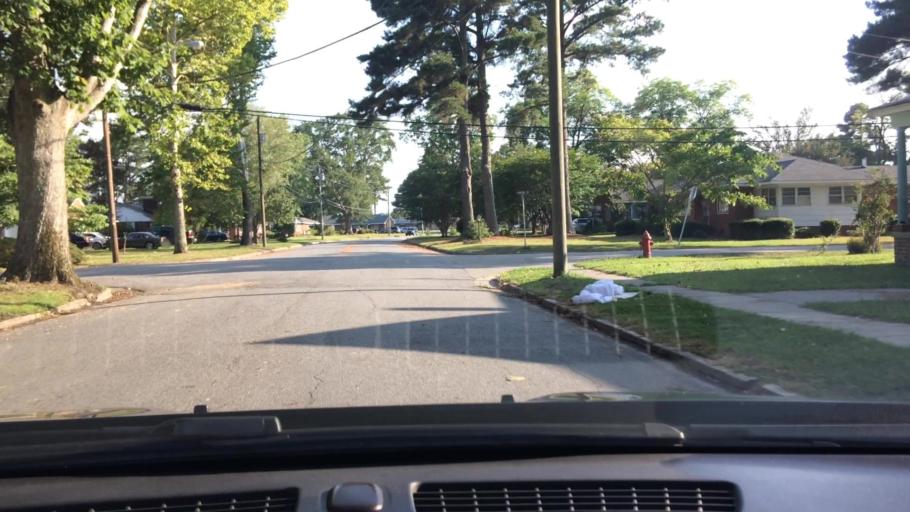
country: US
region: North Carolina
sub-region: Pitt County
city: Ayden
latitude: 35.4684
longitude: -77.4238
